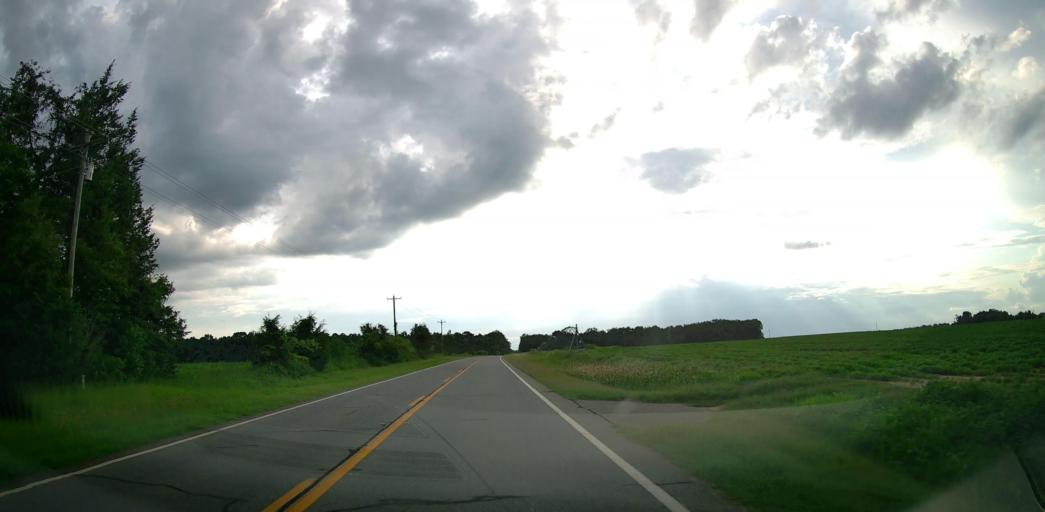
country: US
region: Georgia
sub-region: Pulaski County
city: Hawkinsville
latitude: 32.2955
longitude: -83.5421
